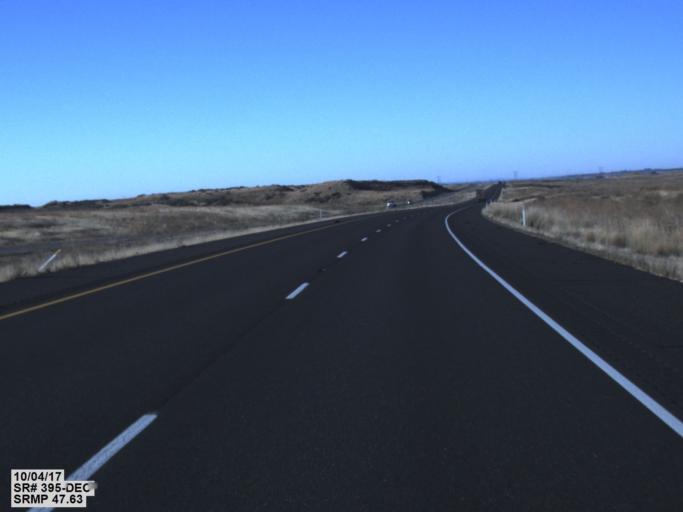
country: US
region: Washington
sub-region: Franklin County
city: Connell
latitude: 46.5851
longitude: -118.9675
